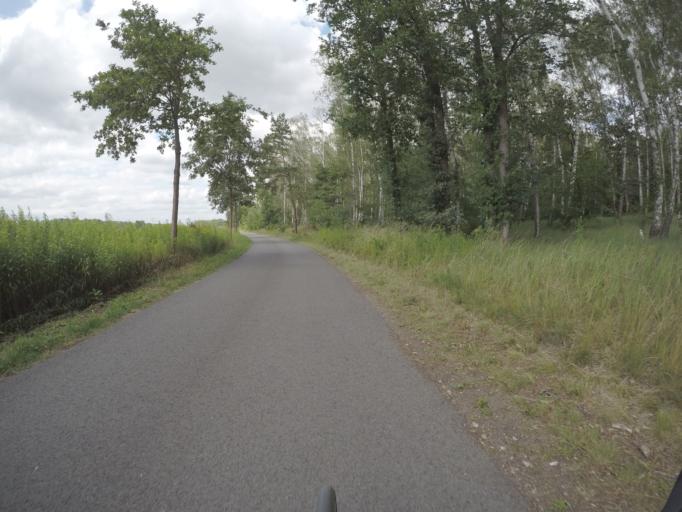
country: DE
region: Brandenburg
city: Falkensee
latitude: 52.6038
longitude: 13.0878
